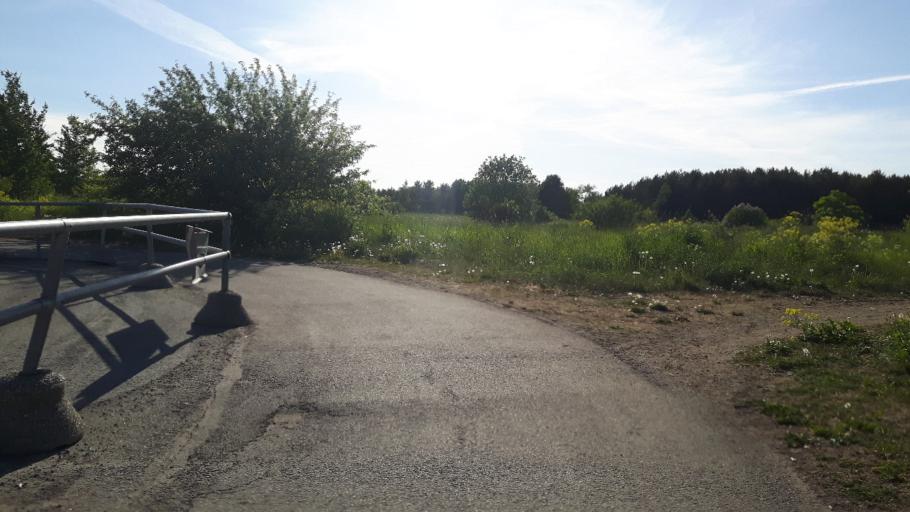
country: EE
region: Harju
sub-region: Viimsi vald
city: Viimsi
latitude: 59.4477
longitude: 24.8242
